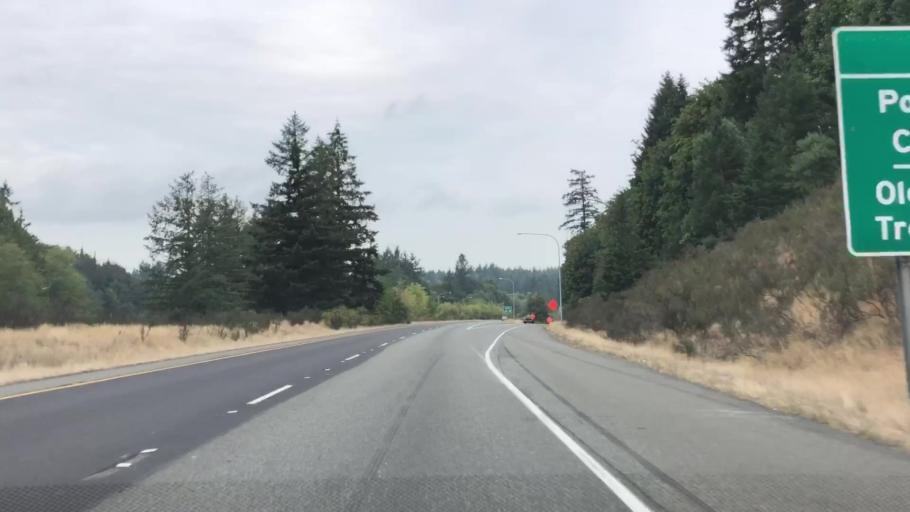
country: US
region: Washington
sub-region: Kitsap County
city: Port Orchard
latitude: 47.5177
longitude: -122.6581
